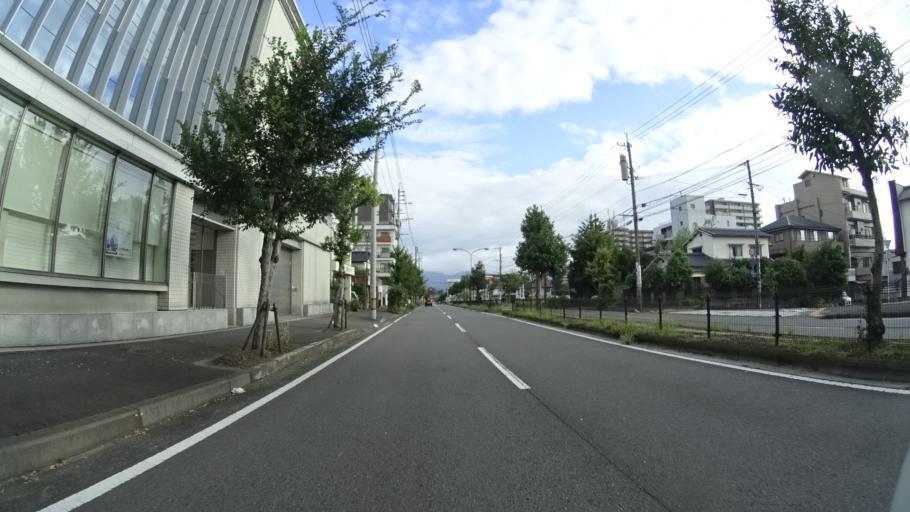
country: JP
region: Oita
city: Beppu
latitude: 33.2998
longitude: 131.4953
